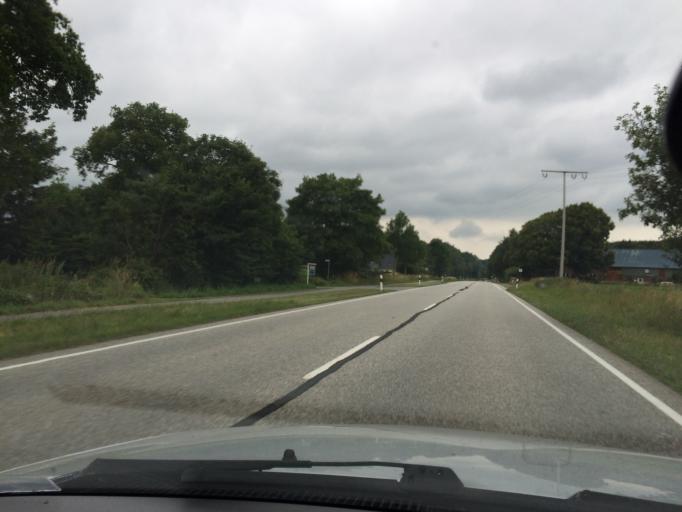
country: DE
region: Schleswig-Holstein
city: Oeversee
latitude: 54.6721
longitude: 9.4411
